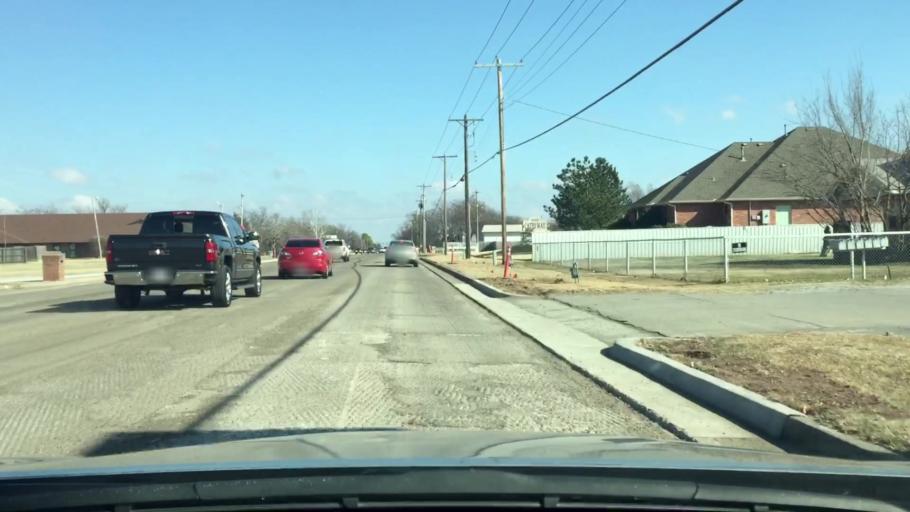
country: US
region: Oklahoma
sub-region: Cleveland County
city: Moore
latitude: 35.3771
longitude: -97.5196
